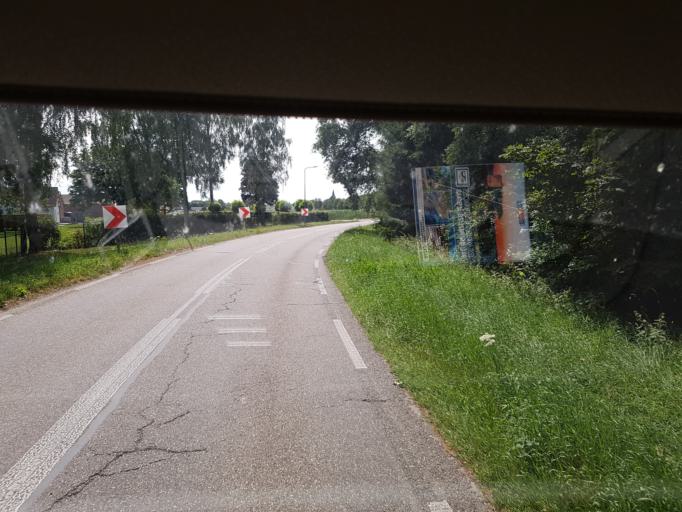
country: NL
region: Limburg
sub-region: Gemeente Leudal
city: Kelpen-Oler
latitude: 51.1959
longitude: 5.8110
